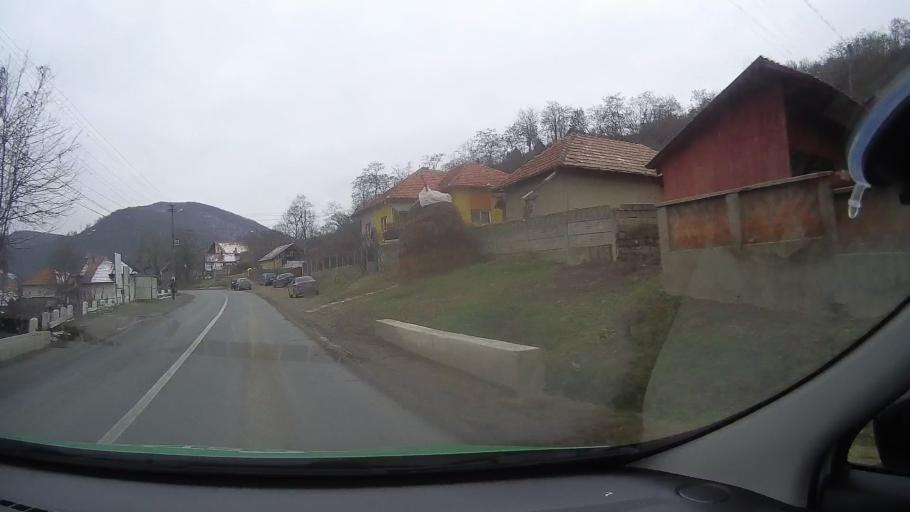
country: RO
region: Alba
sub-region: Comuna Metes
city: Metes
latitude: 46.0986
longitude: 23.4589
